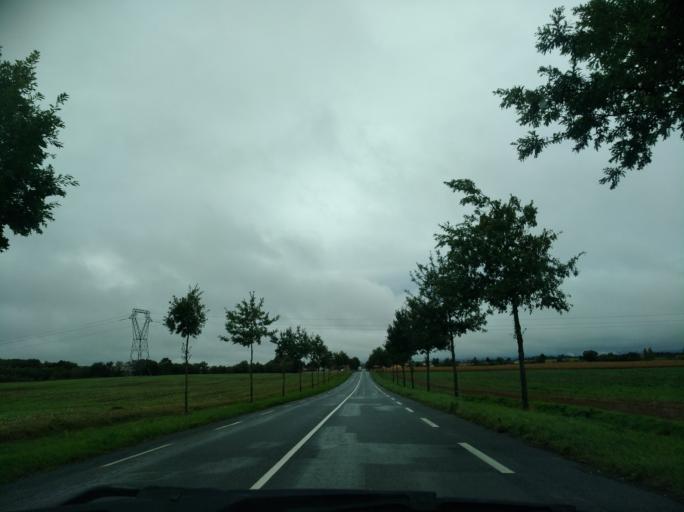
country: FR
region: Rhone-Alpes
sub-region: Departement de l'Ain
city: Chatillon-sur-Chalaronne
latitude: 46.1127
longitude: 4.9163
